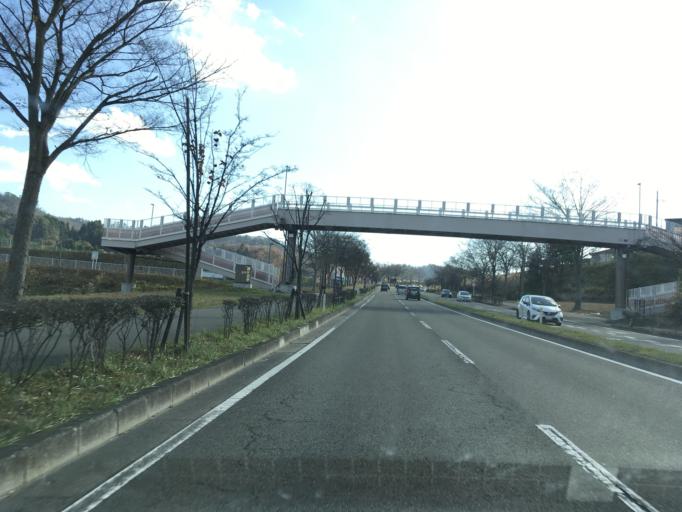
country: JP
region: Miyagi
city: Sendai
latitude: 38.2643
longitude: 140.7617
